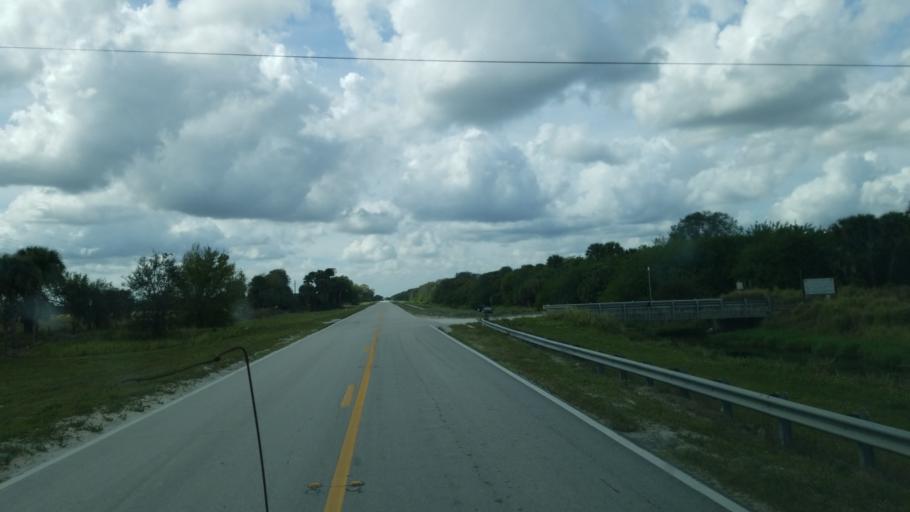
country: US
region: Florida
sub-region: Indian River County
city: West Vero Corridor
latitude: 27.4483
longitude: -80.6116
